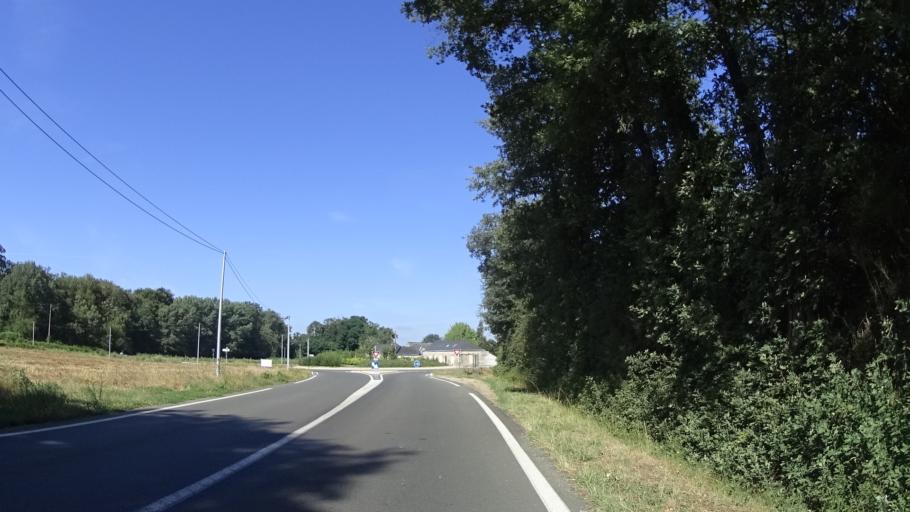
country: FR
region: Pays de la Loire
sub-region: Departement de Maine-et-Loire
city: Etriche
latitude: 47.6384
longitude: -0.4234
